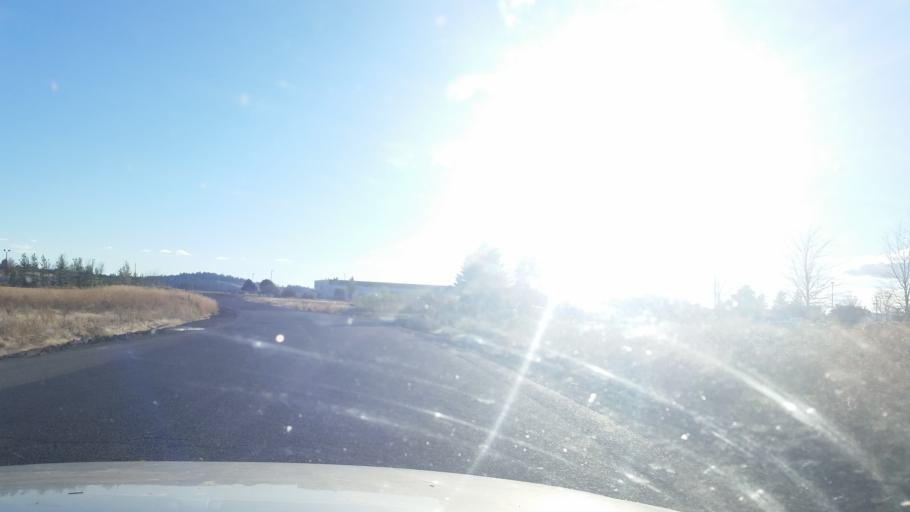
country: US
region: Washington
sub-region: Spokane County
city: Airway Heights
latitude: 47.5868
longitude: -117.5673
